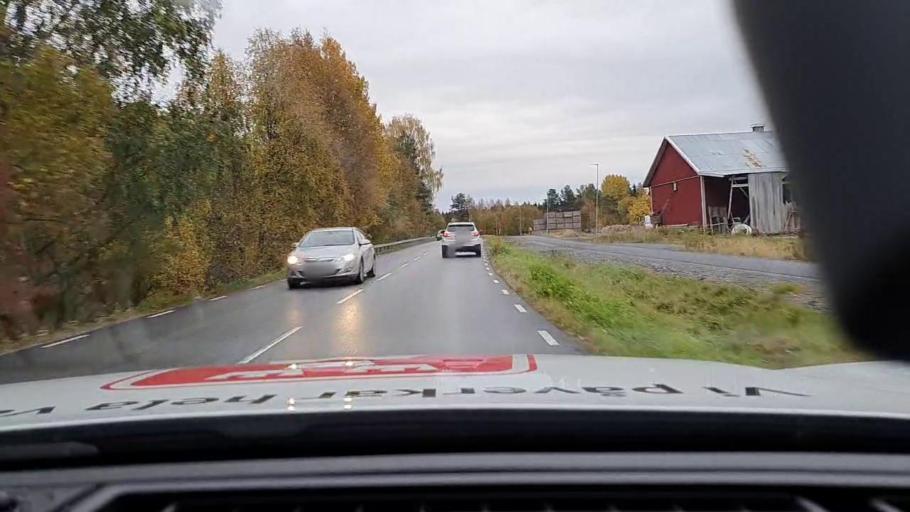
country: SE
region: Norrbotten
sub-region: Bodens Kommun
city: Saevast
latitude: 65.7700
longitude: 21.7054
